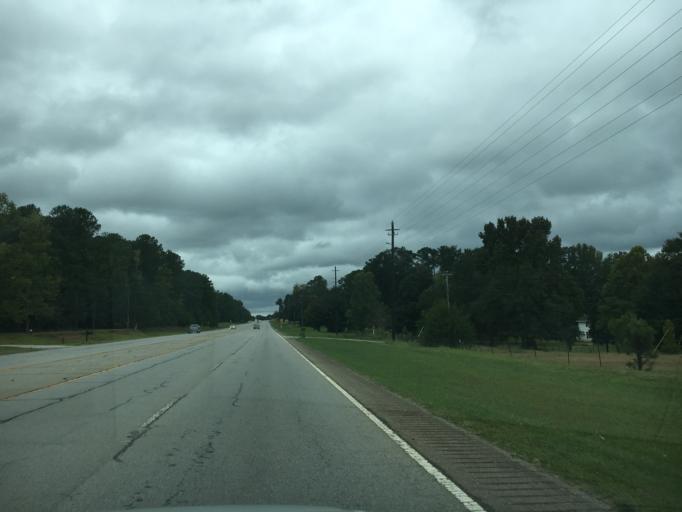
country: US
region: Georgia
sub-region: Wilkes County
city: Washington
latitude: 33.7155
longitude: -82.7037
